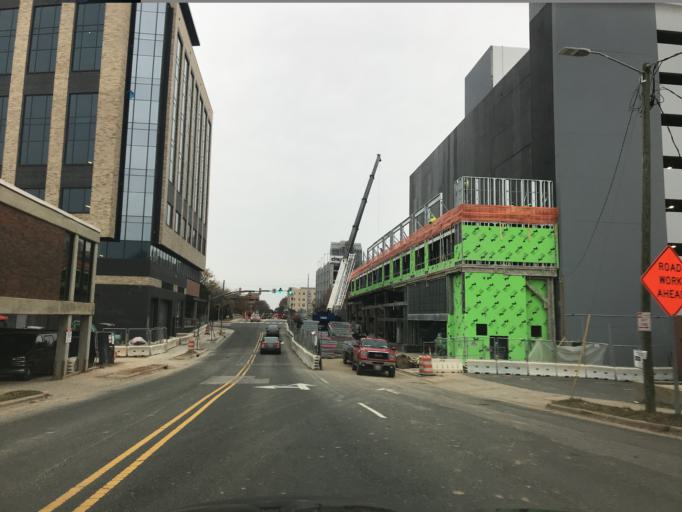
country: US
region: North Carolina
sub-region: Wake County
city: Raleigh
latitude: 35.7800
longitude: -78.6489
